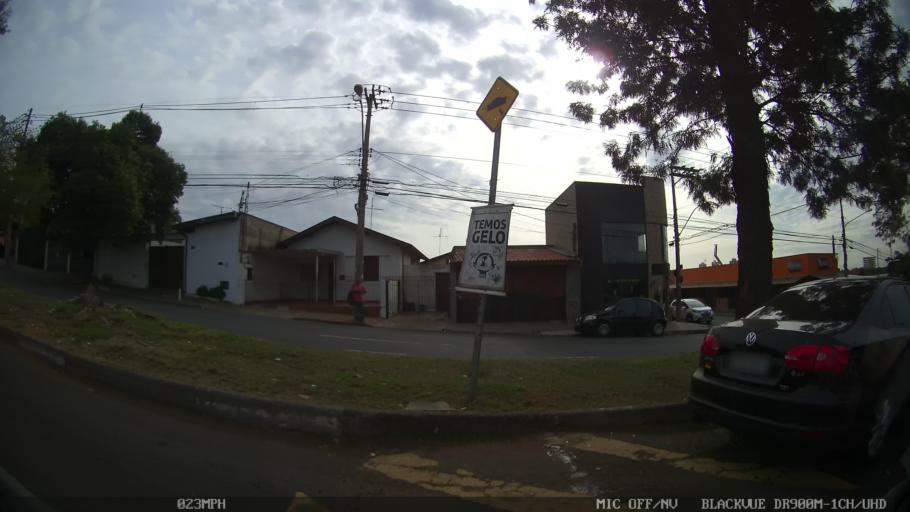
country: BR
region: Sao Paulo
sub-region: Piracicaba
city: Piracicaba
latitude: -22.7351
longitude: -47.6229
